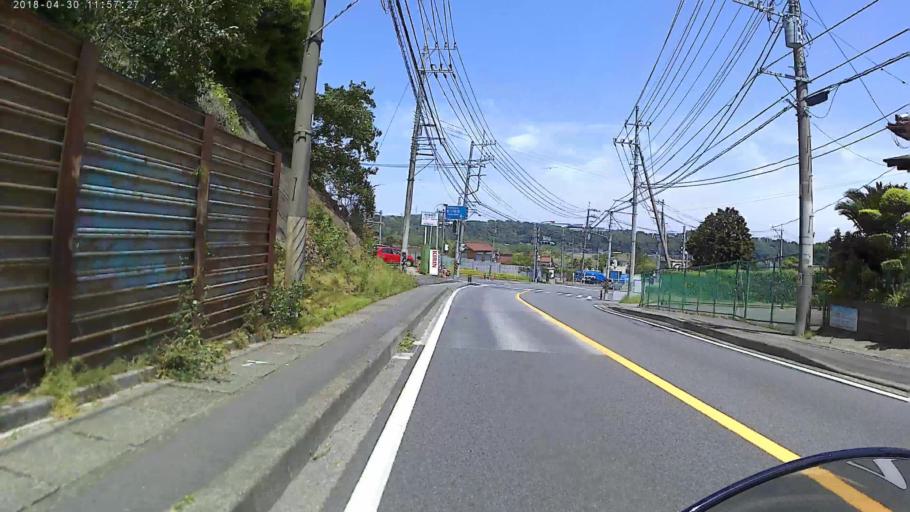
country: JP
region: Kanagawa
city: Zama
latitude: 35.4962
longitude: 139.3413
